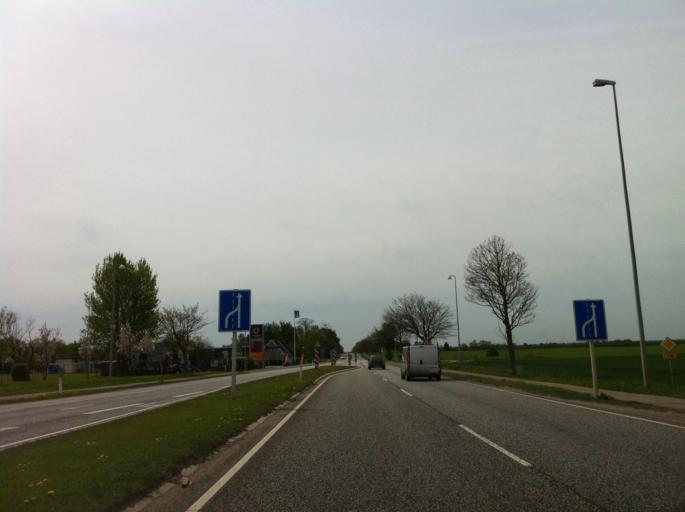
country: DK
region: Zealand
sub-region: Roskilde Kommune
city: Roskilde
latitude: 55.6225
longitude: 12.0567
